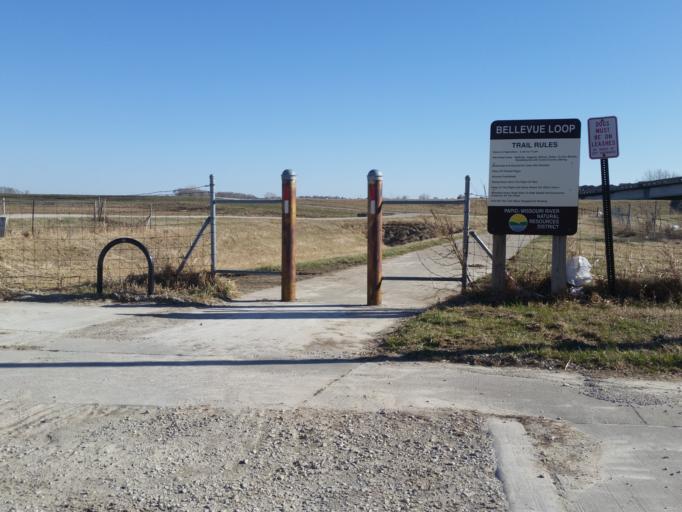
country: US
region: Nebraska
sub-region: Sarpy County
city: Offutt Air Force Base
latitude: 41.1143
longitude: -95.9331
